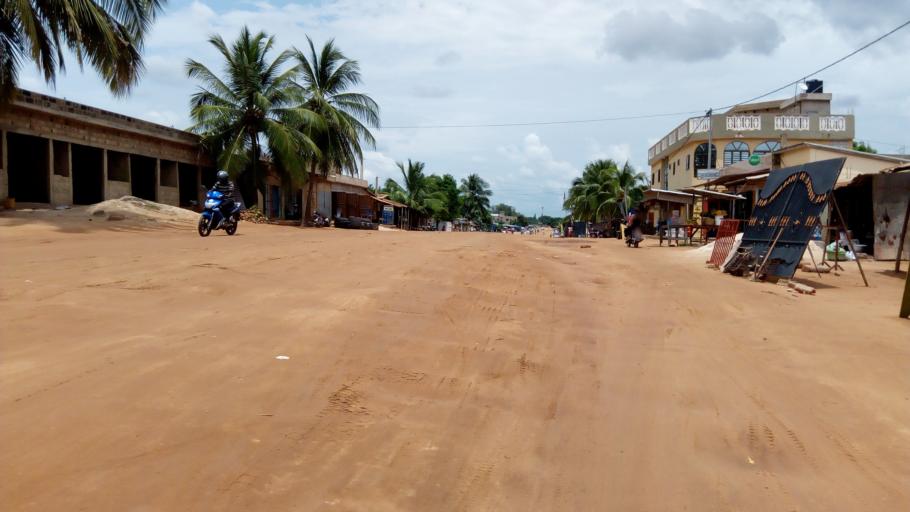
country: TG
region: Maritime
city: Lome
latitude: 6.2272
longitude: 1.1590
